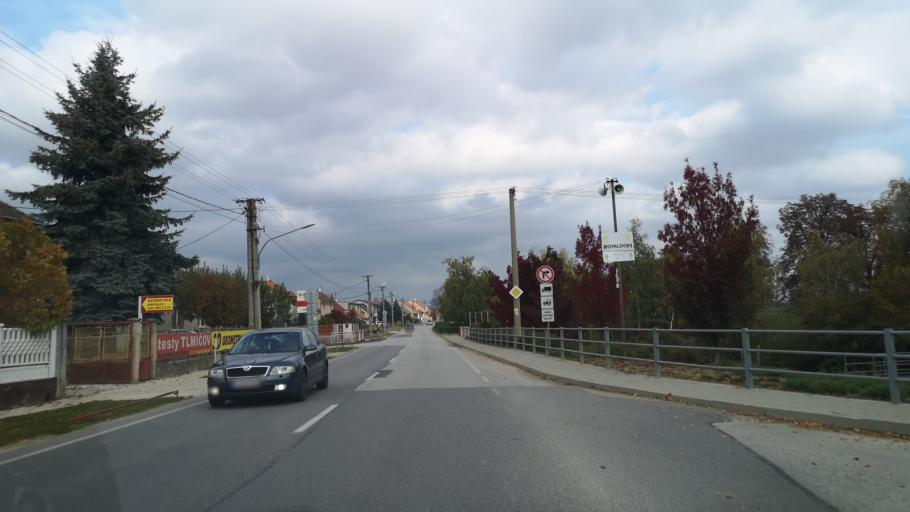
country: SK
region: Nitriansky
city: Cachtice
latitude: 48.6784
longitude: 17.7734
